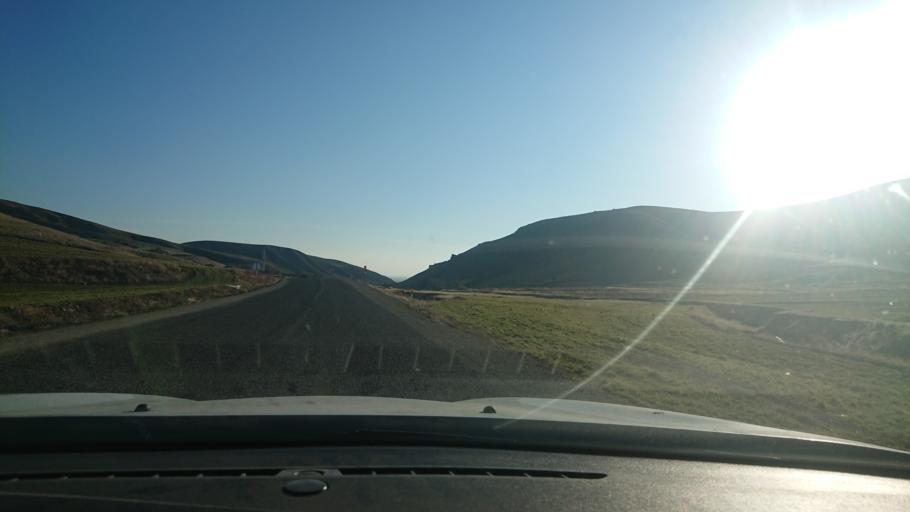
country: TR
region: Aksaray
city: Acipinar
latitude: 38.6970
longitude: 33.7497
